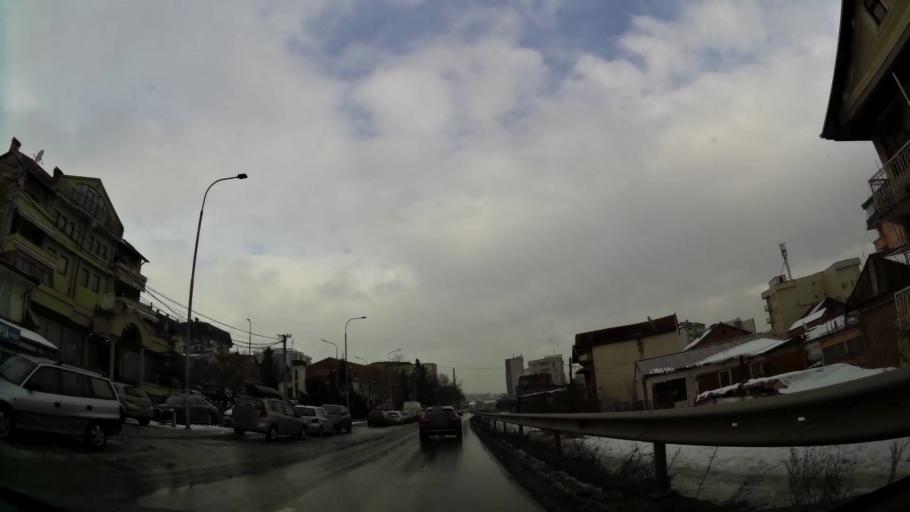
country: XK
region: Pristina
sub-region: Komuna e Prishtines
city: Pristina
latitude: 42.6661
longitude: 21.1559
